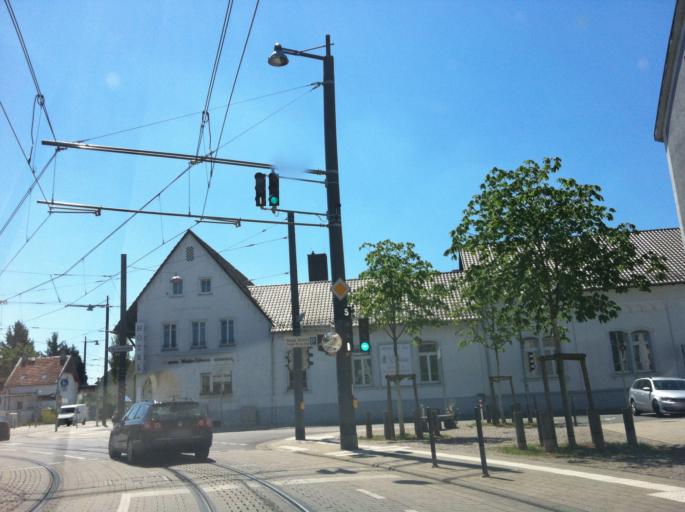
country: DE
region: Hesse
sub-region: Regierungsbezirk Darmstadt
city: Erzhausen
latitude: 49.9140
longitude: 8.6546
